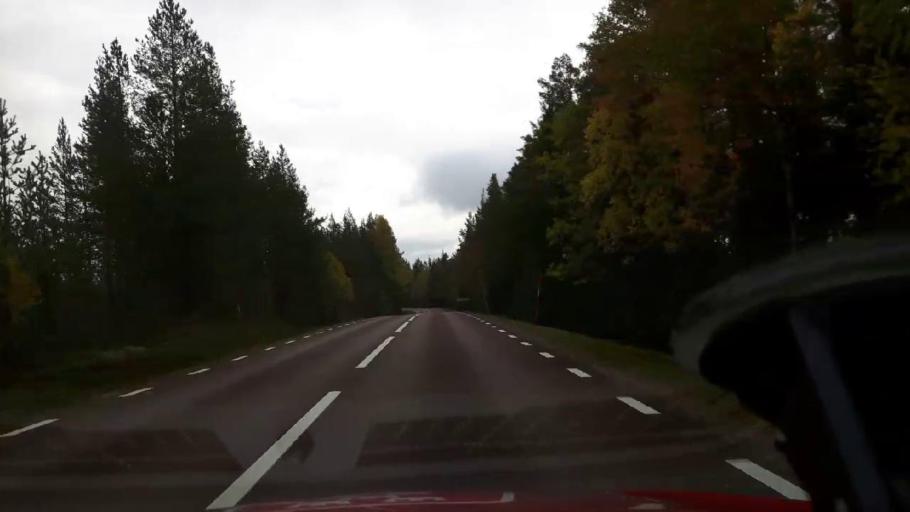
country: SE
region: Jaemtland
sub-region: Harjedalens Kommun
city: Sveg
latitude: 62.1799
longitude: 14.8867
